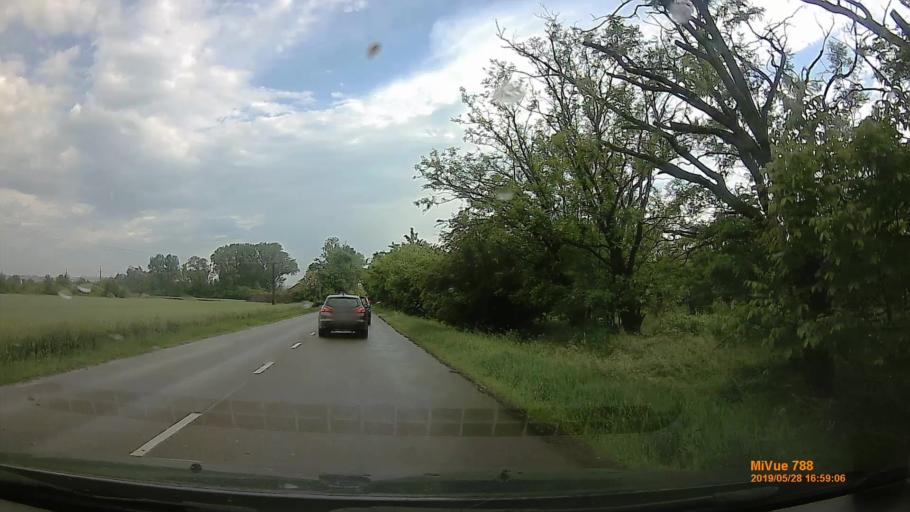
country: HU
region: Pest
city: Nagytarcsa
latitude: 47.5029
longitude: 19.2863
